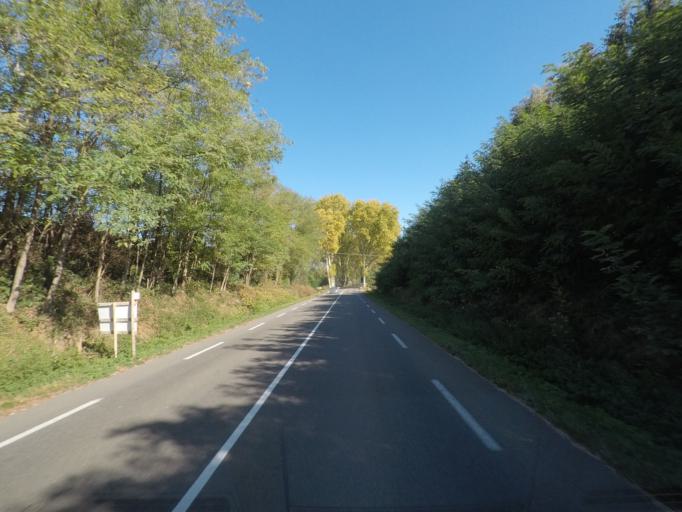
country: FR
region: Rhone-Alpes
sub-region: Departement de l'Ain
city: Servas
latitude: 46.1530
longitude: 5.1801
